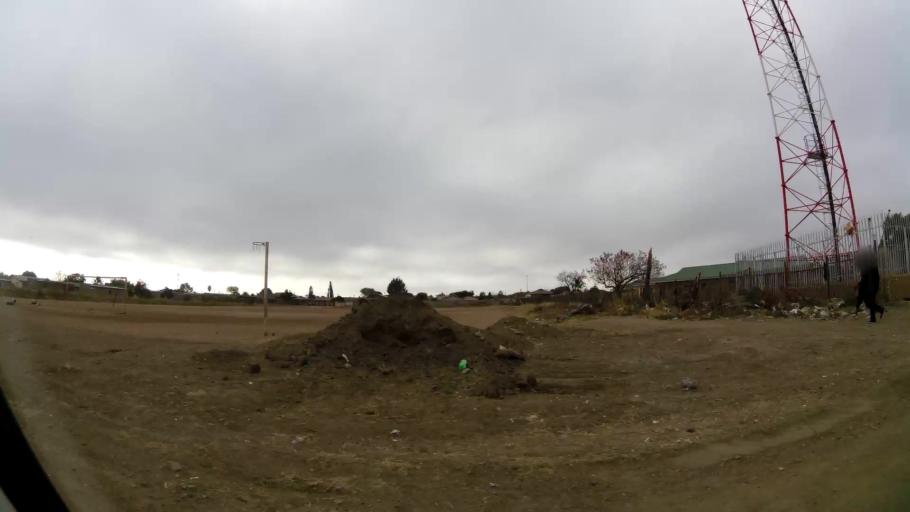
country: ZA
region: Limpopo
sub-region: Capricorn District Municipality
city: Polokwane
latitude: -23.8389
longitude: 29.3887
